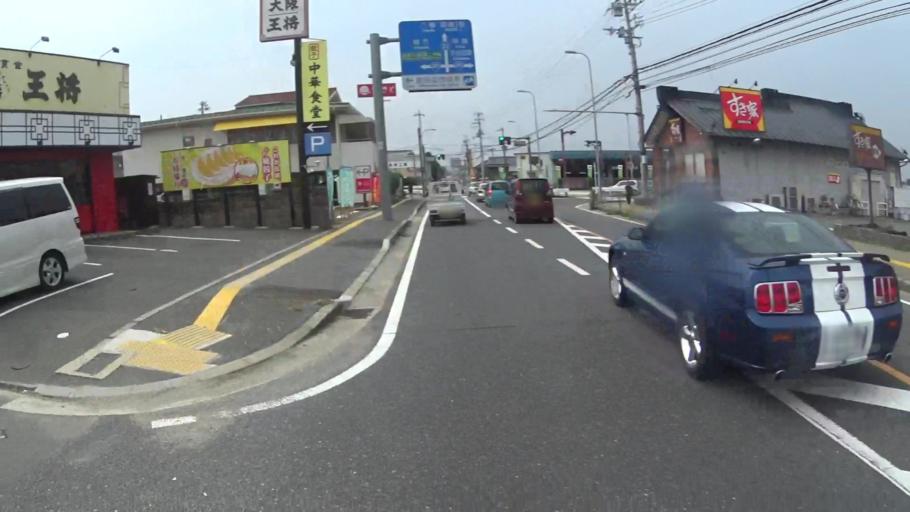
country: JP
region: Kyoto
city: Tanabe
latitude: 34.8133
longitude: 135.7713
